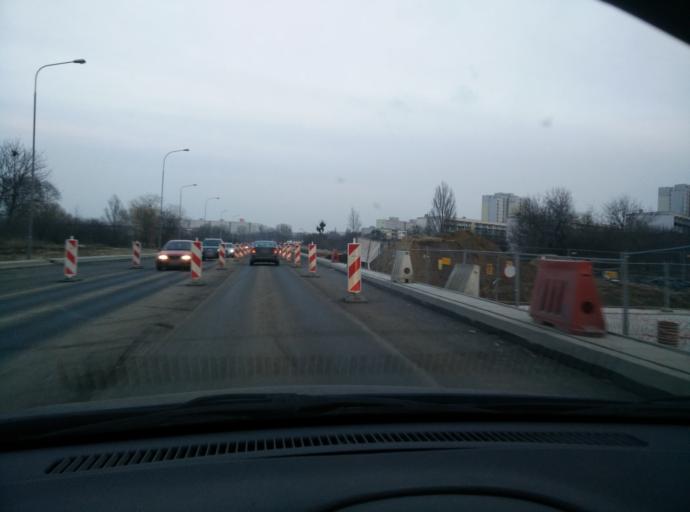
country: PL
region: Greater Poland Voivodeship
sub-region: Poznan
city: Poznan
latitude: 52.3941
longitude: 16.9555
